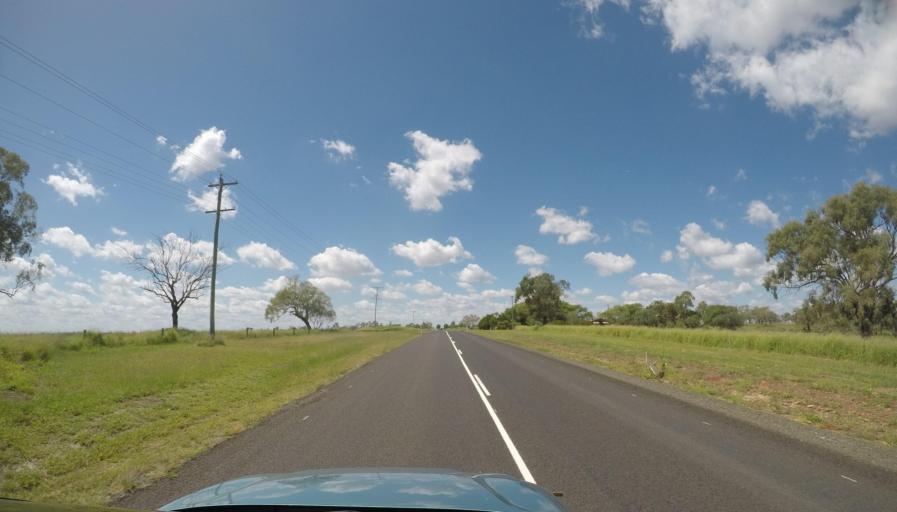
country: AU
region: Queensland
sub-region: Toowoomba
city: Oakey
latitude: -27.5284
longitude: 151.5878
